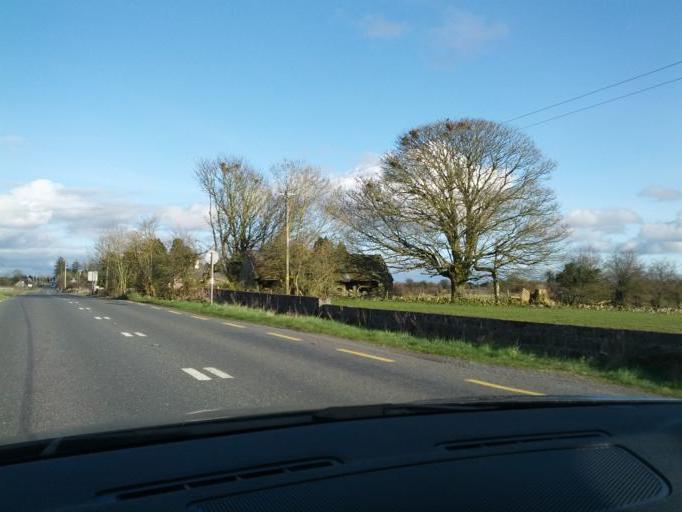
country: IE
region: Connaught
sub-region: Roscommon
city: Roscommon
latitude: 53.6528
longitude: -8.2520
